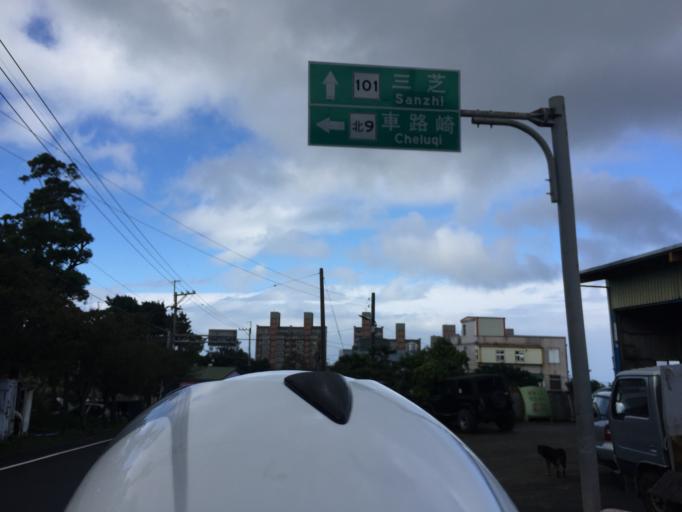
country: TW
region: Taipei
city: Taipei
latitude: 25.2396
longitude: 121.5032
